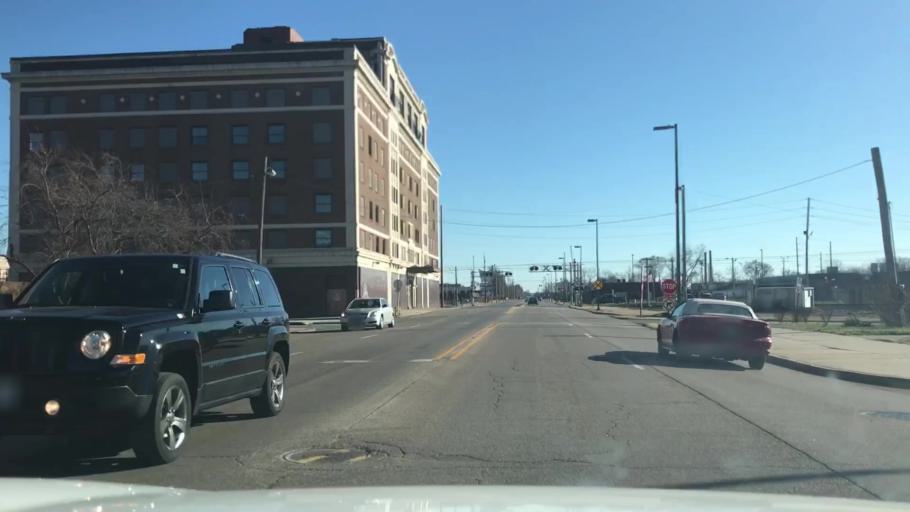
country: US
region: Illinois
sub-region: Saint Clair County
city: East Saint Louis
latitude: 38.6251
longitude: -90.1619
